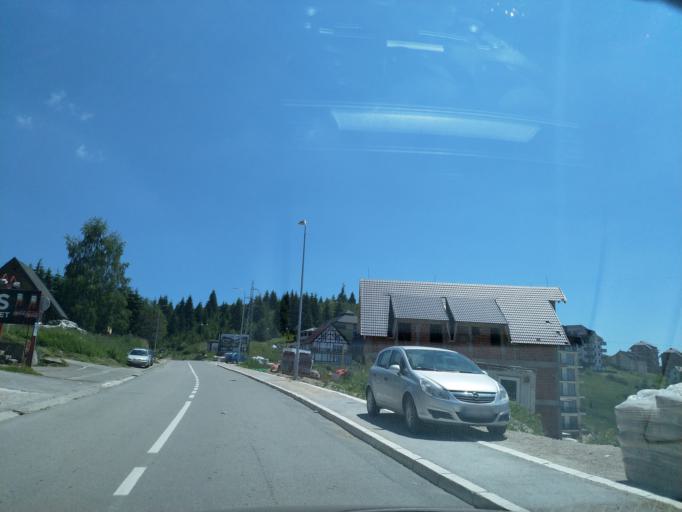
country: RS
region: Central Serbia
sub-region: Raski Okrug
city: Raska
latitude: 43.2743
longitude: 20.7672
